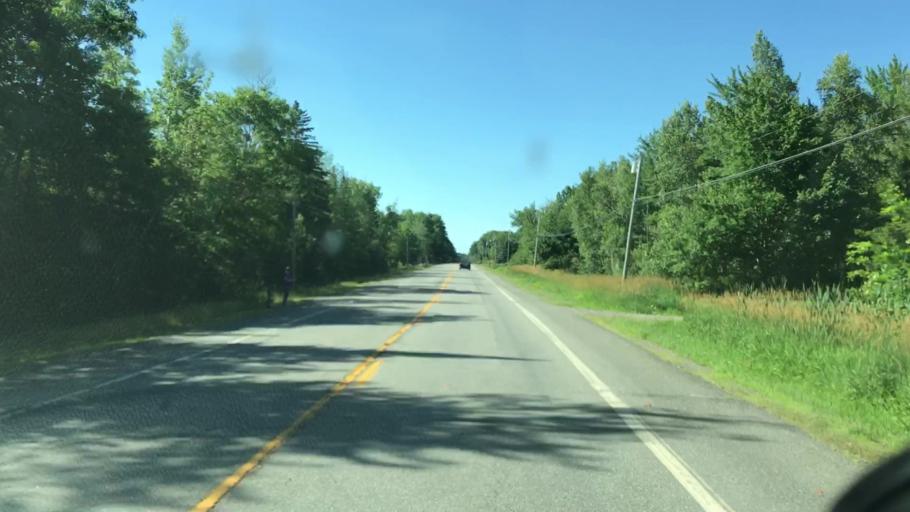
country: US
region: Maine
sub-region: Penobscot County
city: Howland
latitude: 45.2684
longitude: -68.6388
